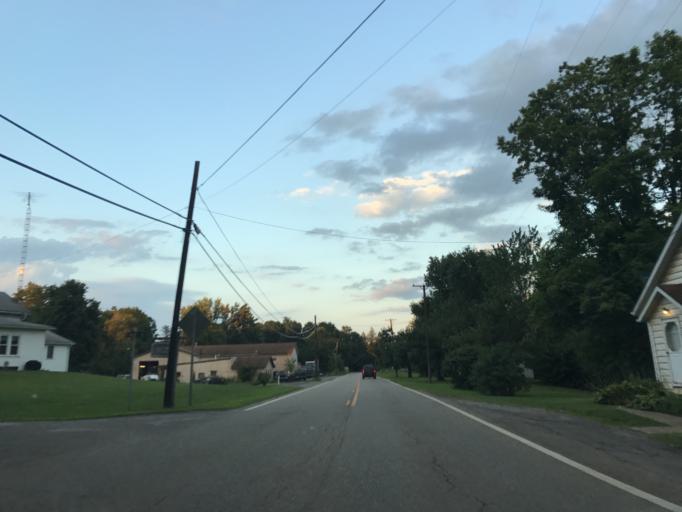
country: US
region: Ohio
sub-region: Columbiana County
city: Salineville
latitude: 40.7518
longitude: -80.9344
